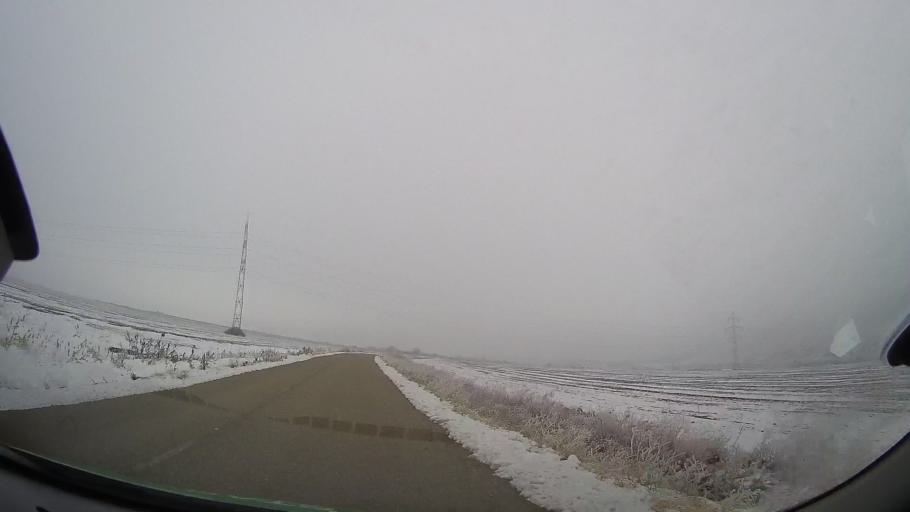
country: RO
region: Vaslui
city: Coroiesti
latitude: 46.2358
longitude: 27.4777
